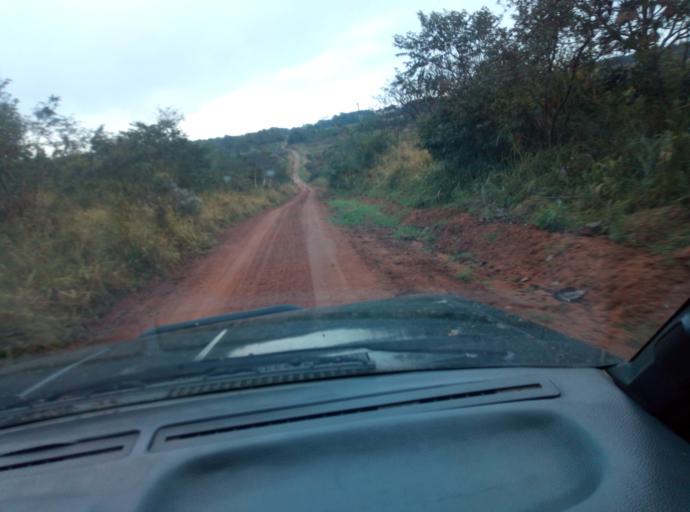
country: PY
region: Caaguazu
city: Carayao
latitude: -25.1904
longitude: -56.3481
